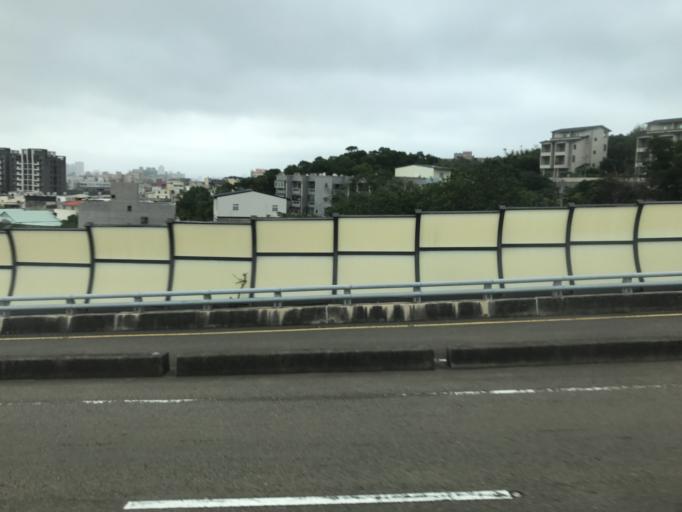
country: TW
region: Taiwan
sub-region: Hsinchu
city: Hsinchu
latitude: 24.7919
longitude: 120.9463
